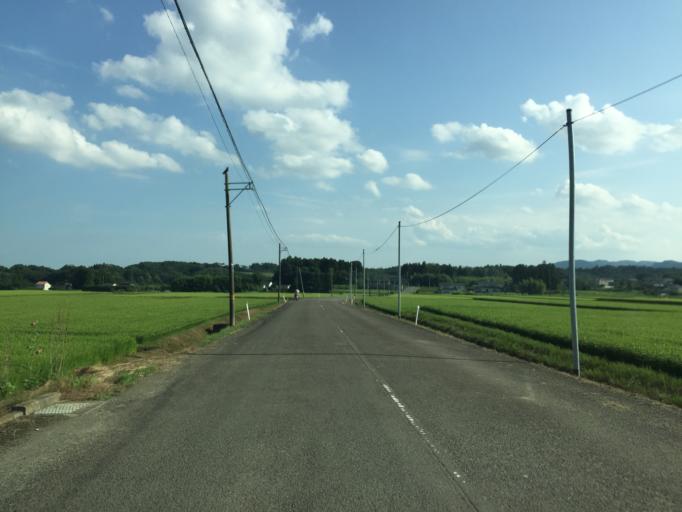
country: JP
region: Miyagi
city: Marumori
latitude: 37.8050
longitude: 140.8949
